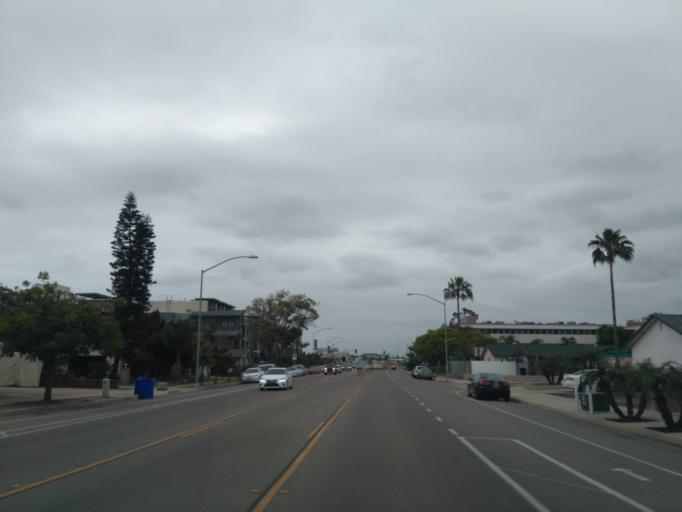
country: US
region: California
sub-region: San Diego County
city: San Diego
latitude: 32.8074
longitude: -117.1401
